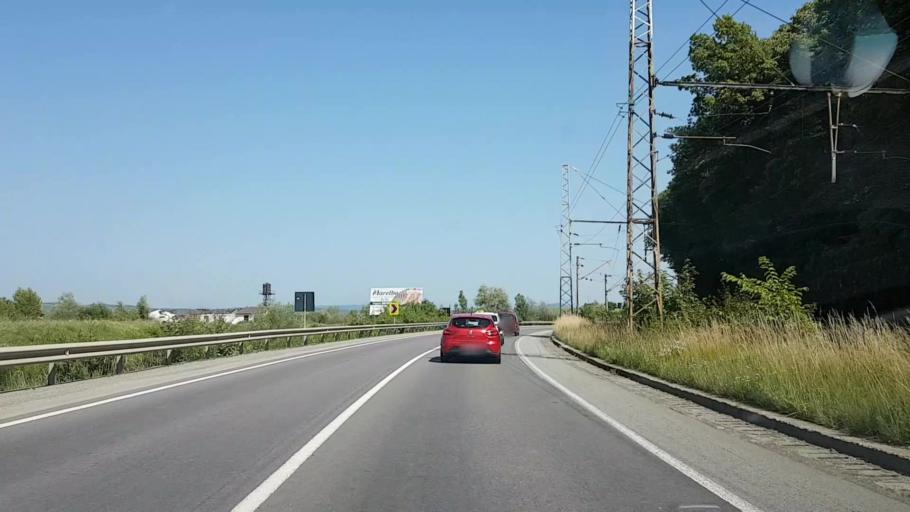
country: RO
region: Bistrita-Nasaud
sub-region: Comuna Beclean
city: Beclean
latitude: 47.1866
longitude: 24.1991
